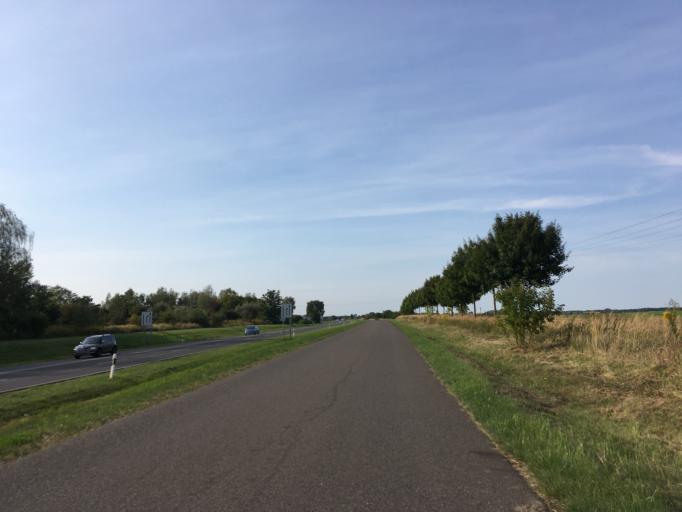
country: DE
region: Brandenburg
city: Brieskow-Finkenheerd
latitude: 52.2724
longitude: 14.5660
